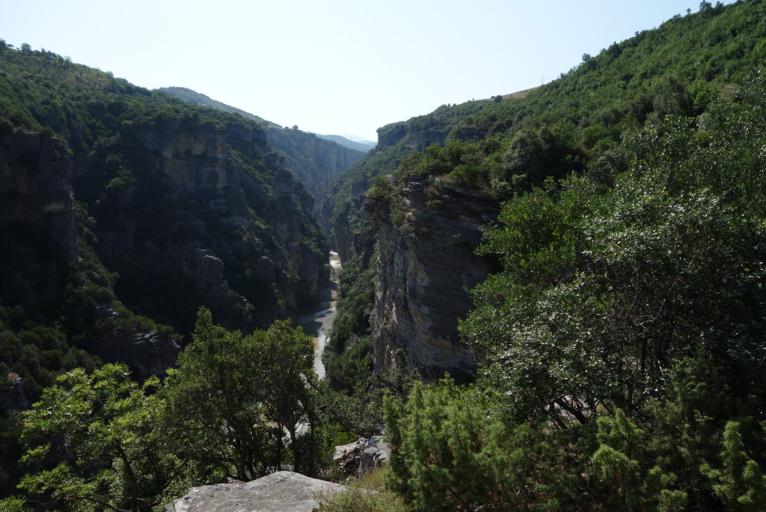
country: AL
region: Berat
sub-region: Rrethi i Skraparit
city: Corovode
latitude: 40.4879
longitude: 20.2296
